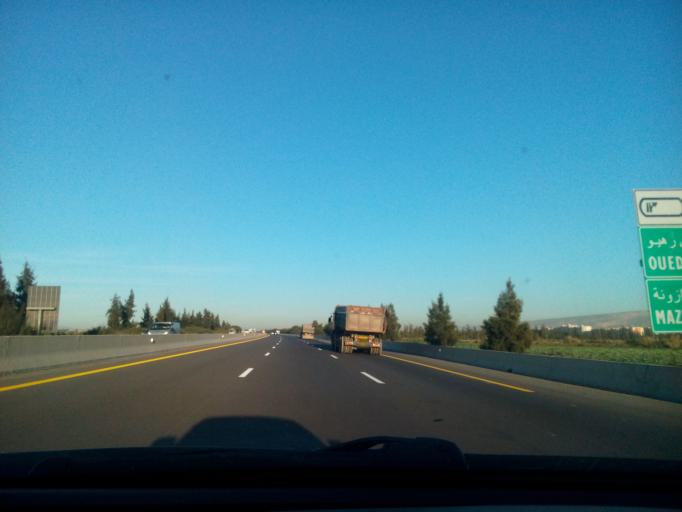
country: DZ
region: Relizane
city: Oued Rhiou
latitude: 35.9609
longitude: 0.8874
